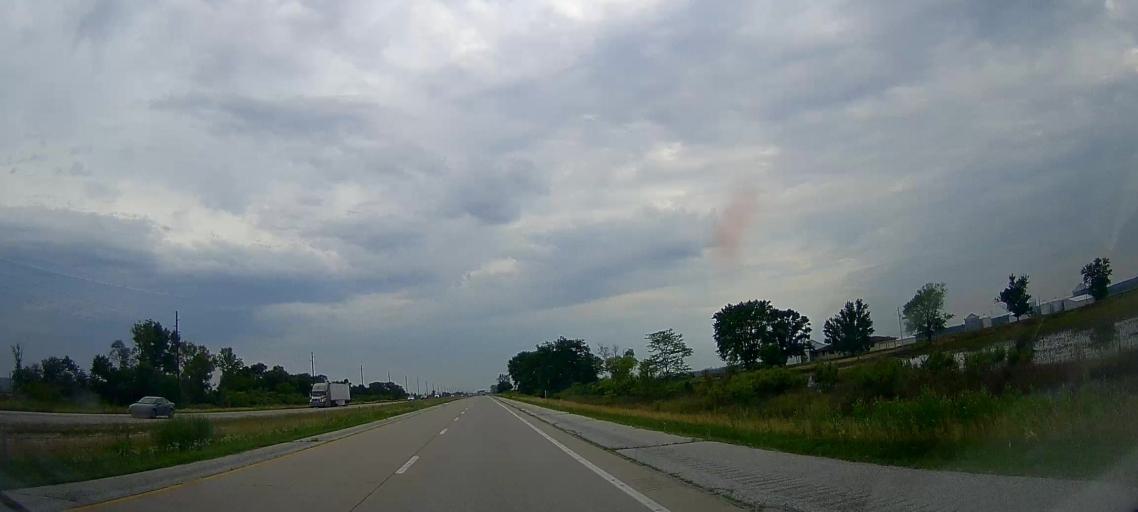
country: US
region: Iowa
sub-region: Pottawattamie County
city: Carter Lake
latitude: 41.3955
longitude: -95.8997
